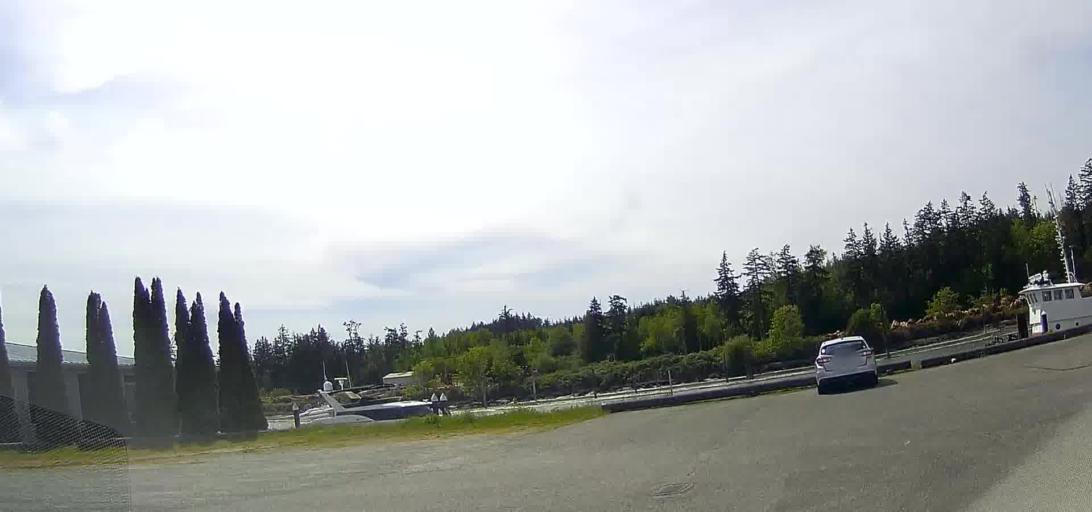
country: US
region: Washington
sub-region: Skagit County
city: Mount Vernon
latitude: 48.3981
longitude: -122.4958
